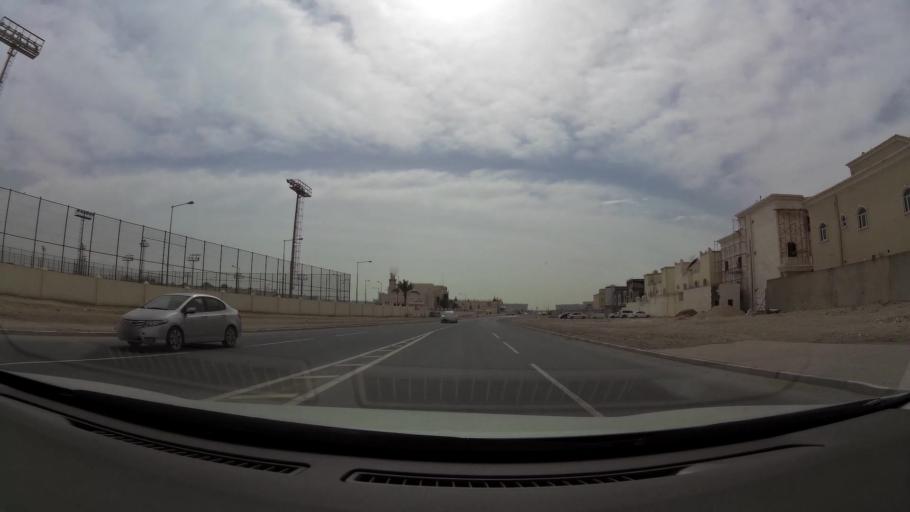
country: QA
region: Baladiyat ad Dawhah
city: Doha
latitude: 25.2217
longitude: 51.4917
